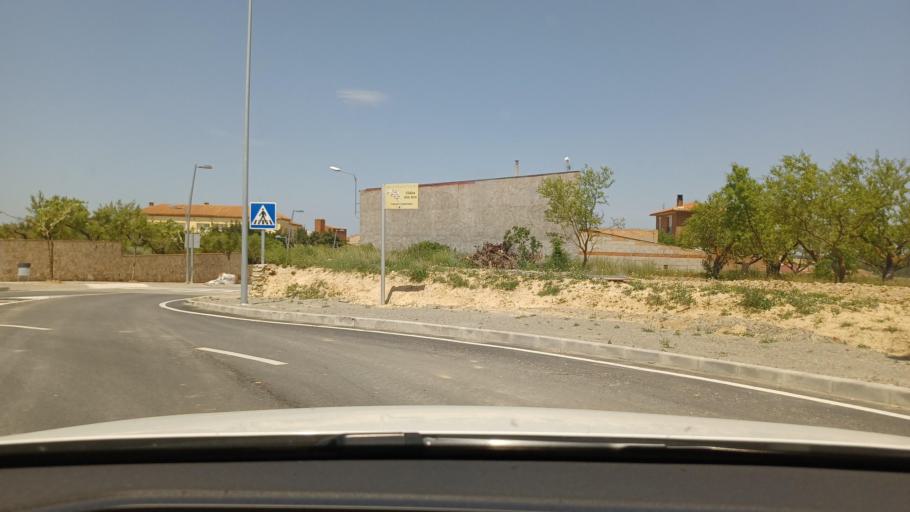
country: ES
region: Catalonia
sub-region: Provincia de Tarragona
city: Vilalba dels Arcs
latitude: 41.1171
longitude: 0.4092
